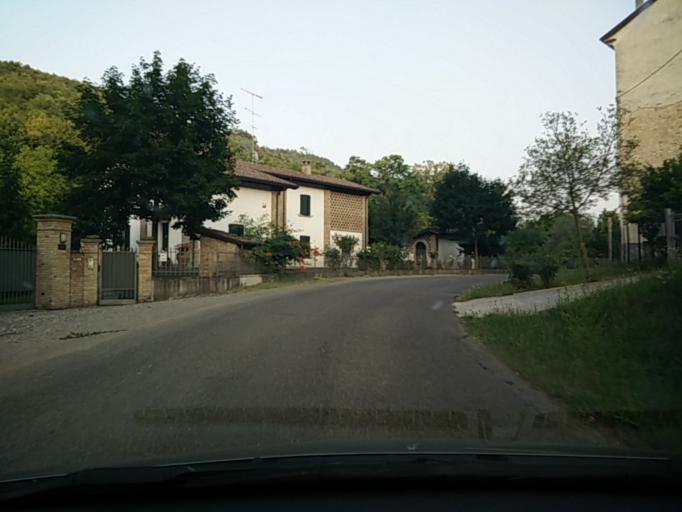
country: IT
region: Lombardy
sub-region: Provincia di Pavia
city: Susella
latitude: 44.9510
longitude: 9.1062
